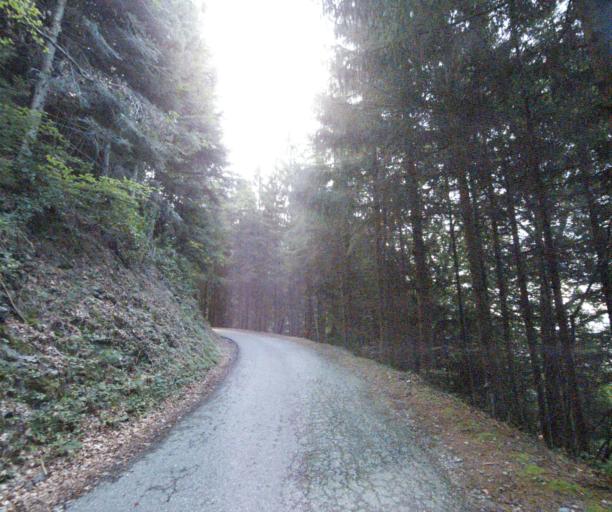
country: CH
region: Vaud
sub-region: Aigle District
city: Villeneuve
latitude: 46.4085
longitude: 6.9398
